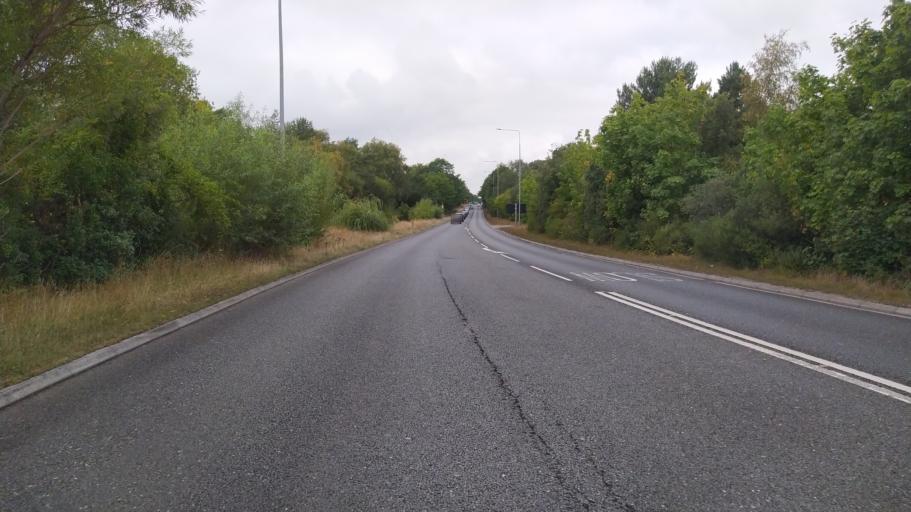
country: GB
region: England
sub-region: Bournemouth
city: Bournemouth
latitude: 50.7226
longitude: -1.8952
